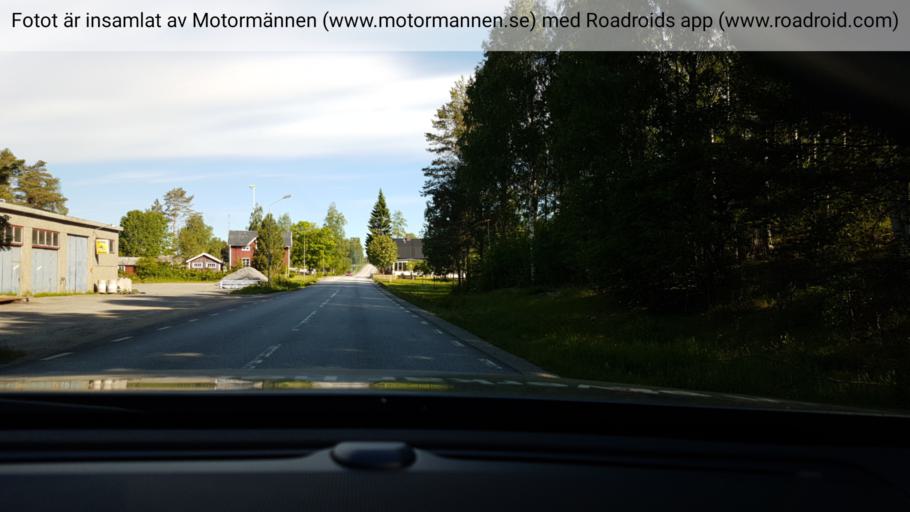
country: SE
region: Vaesterbotten
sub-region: Vindelns Kommun
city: Vindeln
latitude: 64.1529
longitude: 19.5107
